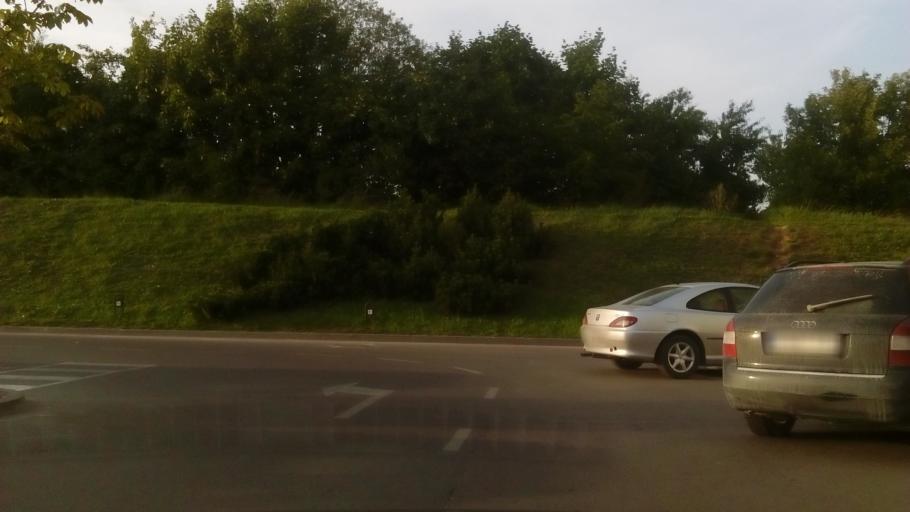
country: LT
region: Alytaus apskritis
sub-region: Alytus
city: Alytus
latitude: 54.3879
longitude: 24.0269
